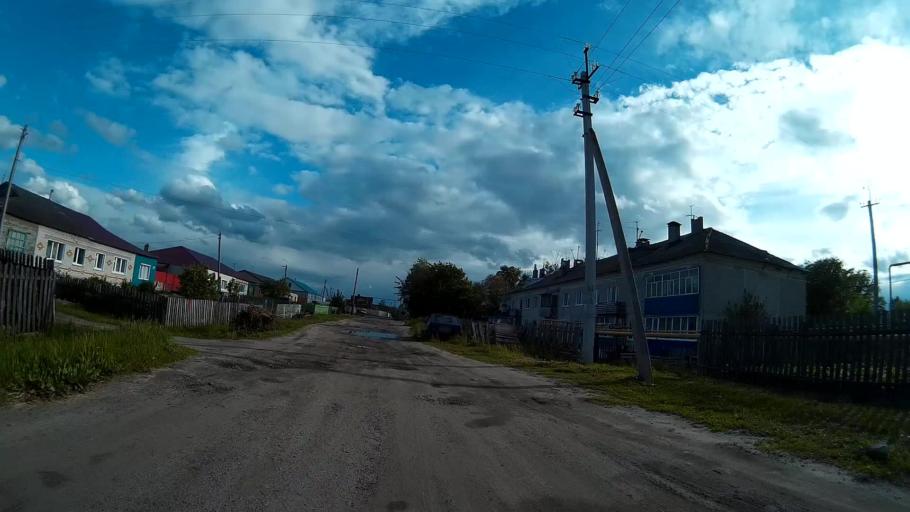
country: RU
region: Ulyanovsk
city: Novoul'yanovsk
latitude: 54.2024
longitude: 48.2687
